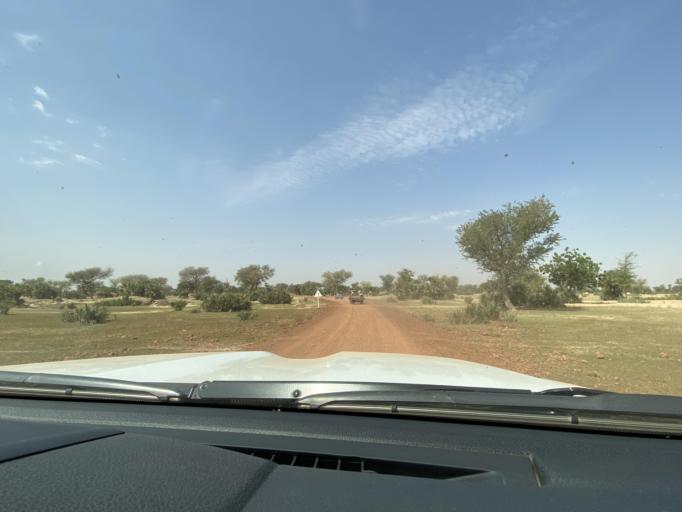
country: NE
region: Dosso
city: Birnin Gaoure
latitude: 13.2468
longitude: 2.8577
